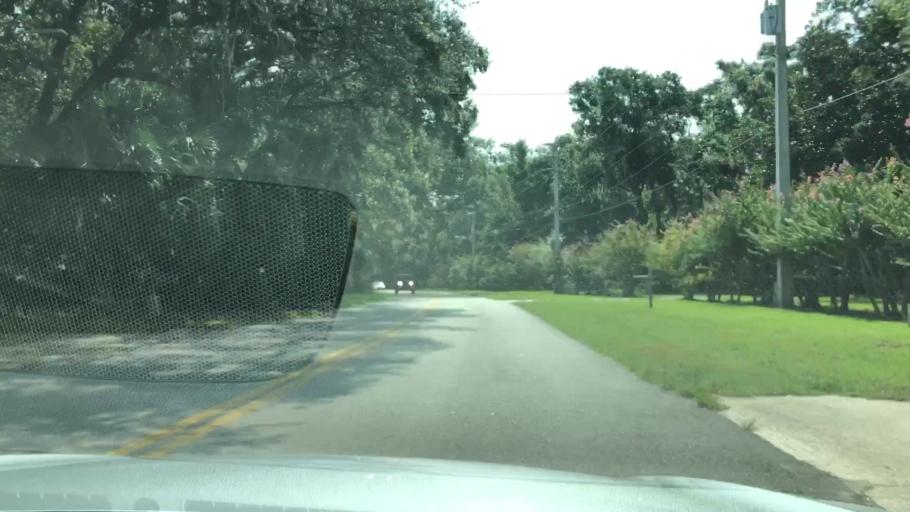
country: US
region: Florida
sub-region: Duval County
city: Neptune Beach
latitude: 30.3146
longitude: -81.4069
